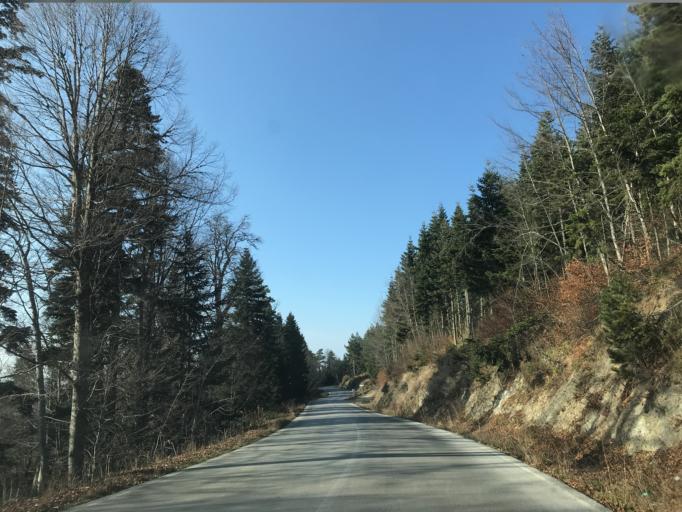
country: TR
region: Bolu
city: Bolu
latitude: 40.8881
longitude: 31.6790
